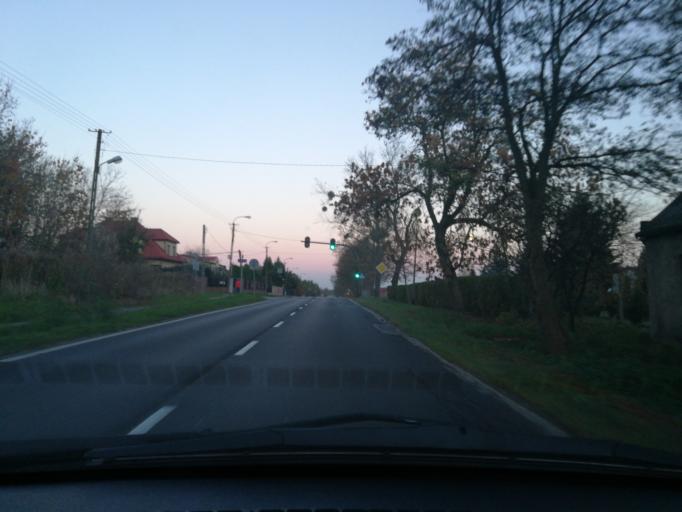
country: PL
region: Lodz Voivodeship
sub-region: Powiat lodzki wschodni
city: Andrespol
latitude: 51.7932
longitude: 19.6000
